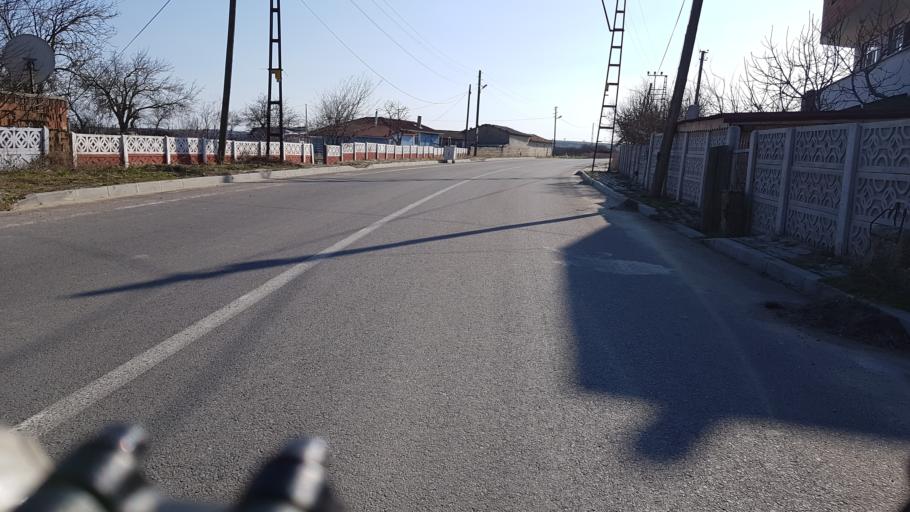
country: TR
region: Tekirdag
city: Saray
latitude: 41.3696
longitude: 27.8620
